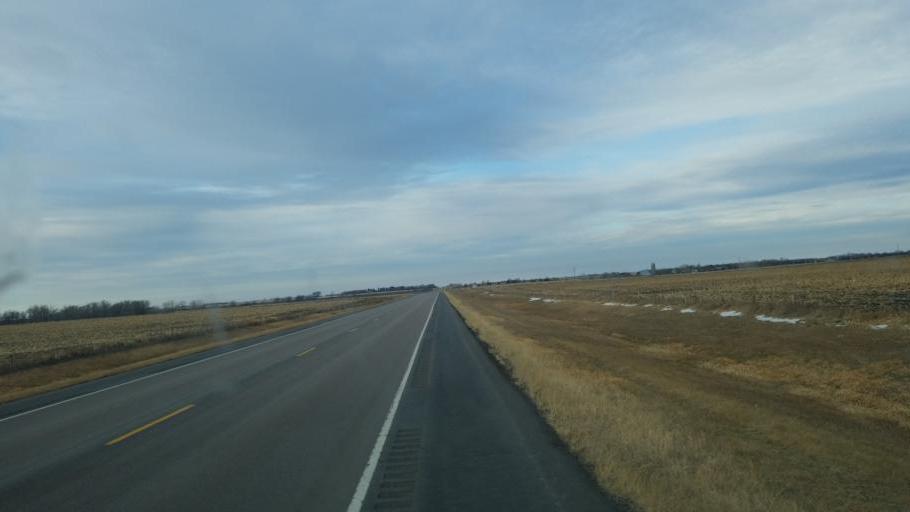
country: US
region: South Dakota
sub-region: Hutchinson County
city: Olivet
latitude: 43.0823
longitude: -97.6512
